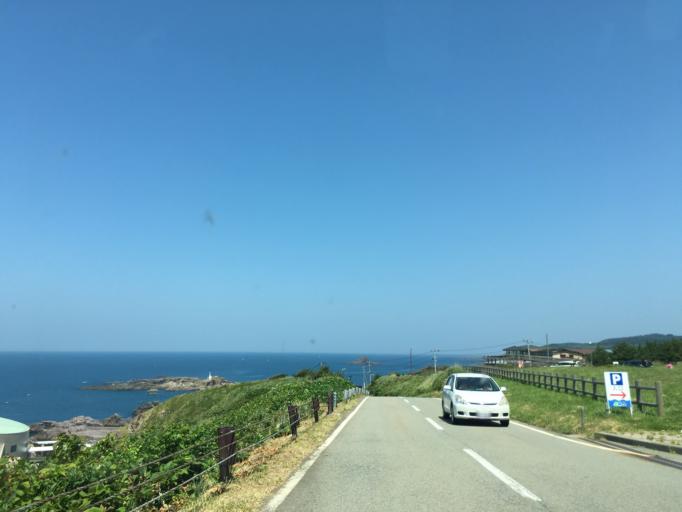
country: JP
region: Akita
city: Tenno
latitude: 39.9410
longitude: 139.7067
